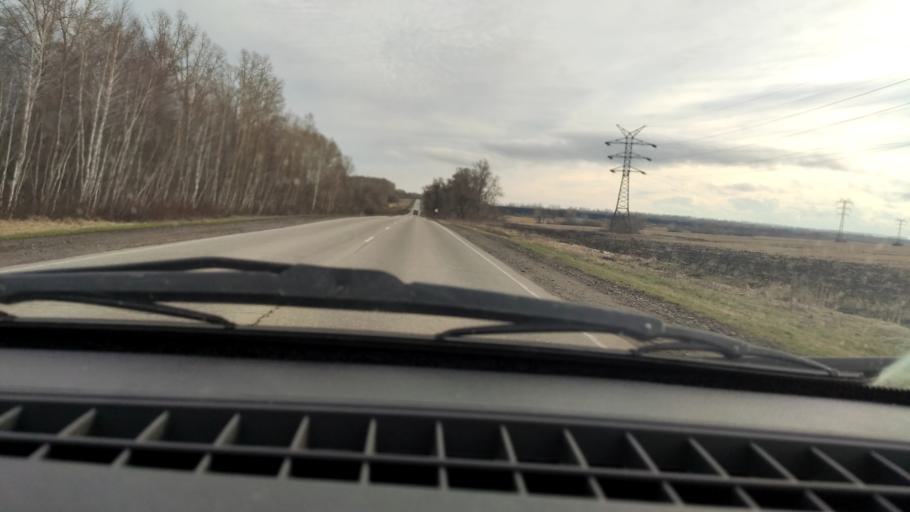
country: RU
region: Bashkortostan
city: Chishmy
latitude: 54.5170
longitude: 55.2956
